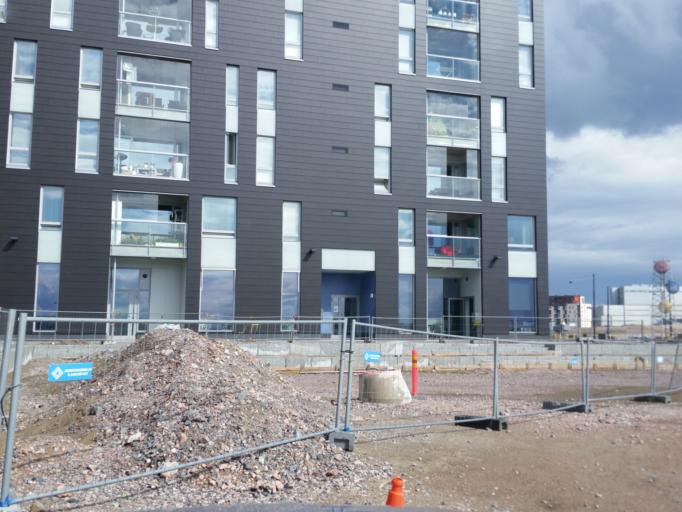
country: FI
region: Uusimaa
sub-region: Helsinki
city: Helsinki
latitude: 60.1577
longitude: 24.9089
